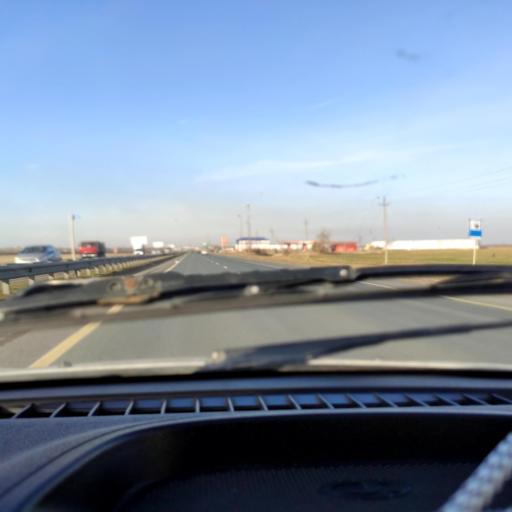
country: RU
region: Samara
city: Zhigulevsk
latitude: 53.5523
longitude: 49.5060
